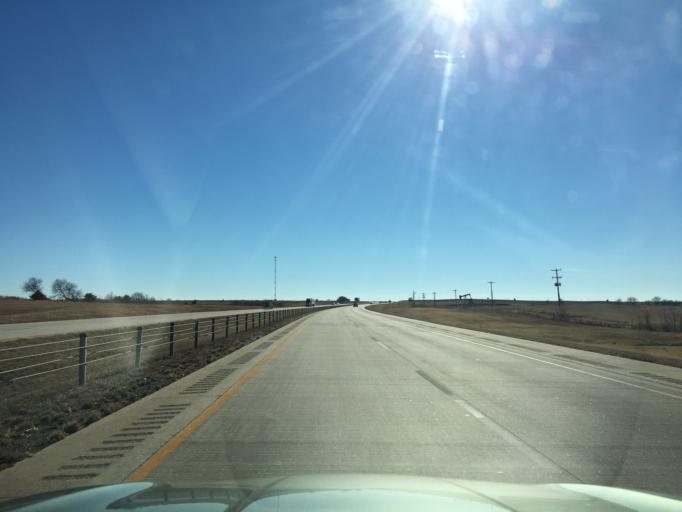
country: US
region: Oklahoma
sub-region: Kay County
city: Tonkawa
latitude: 36.5202
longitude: -97.3380
